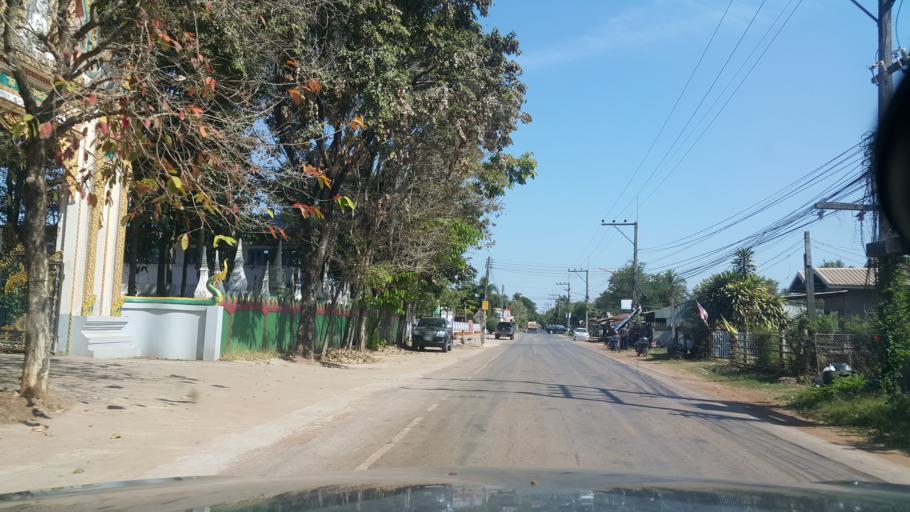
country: TH
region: Changwat Udon Thani
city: Udon Thani
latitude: 17.5066
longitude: 102.7585
